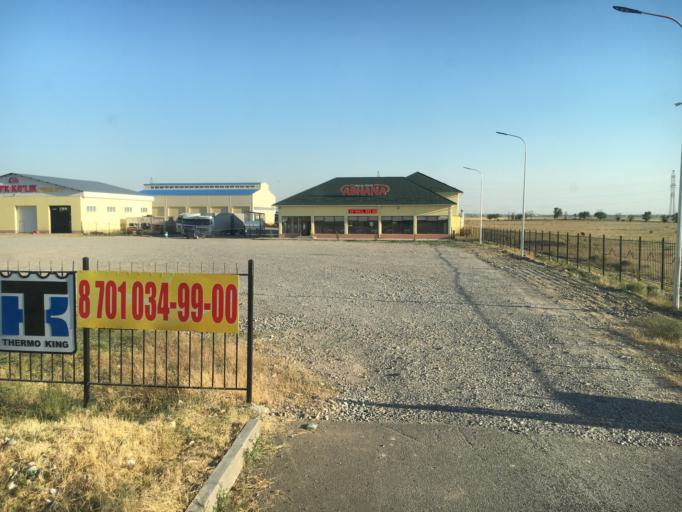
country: KZ
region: Ongtustik Qazaqstan
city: Shymkent
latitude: 42.4540
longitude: 69.6174
